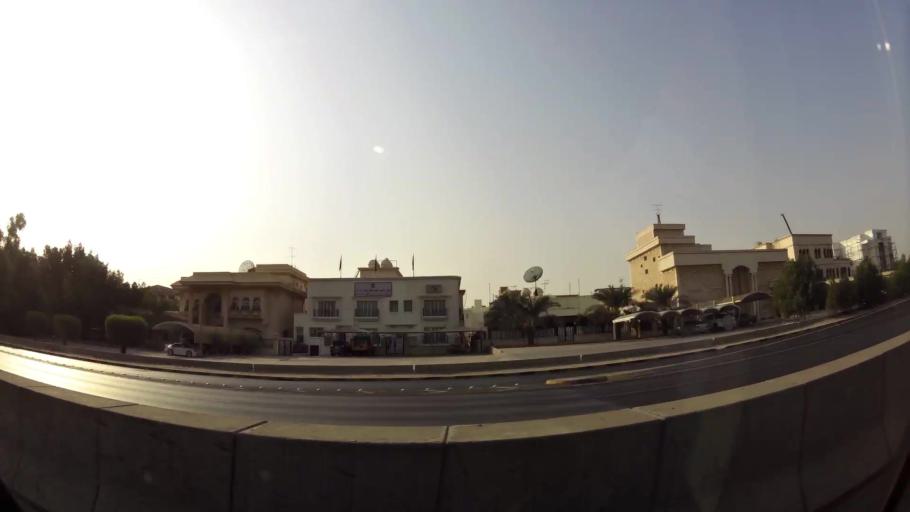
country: KW
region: Al Asimah
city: Ash Shamiyah
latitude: 29.3189
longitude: 47.9773
